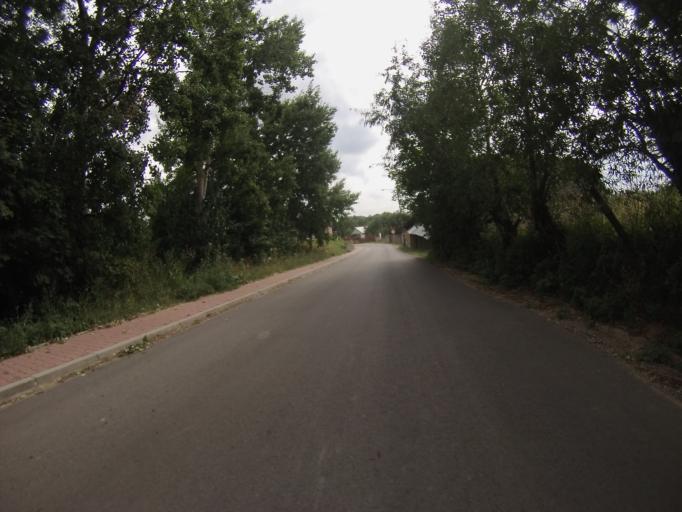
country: PL
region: Swietokrzyskie
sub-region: Powiat kielecki
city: Lagow
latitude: 50.7262
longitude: 21.1057
